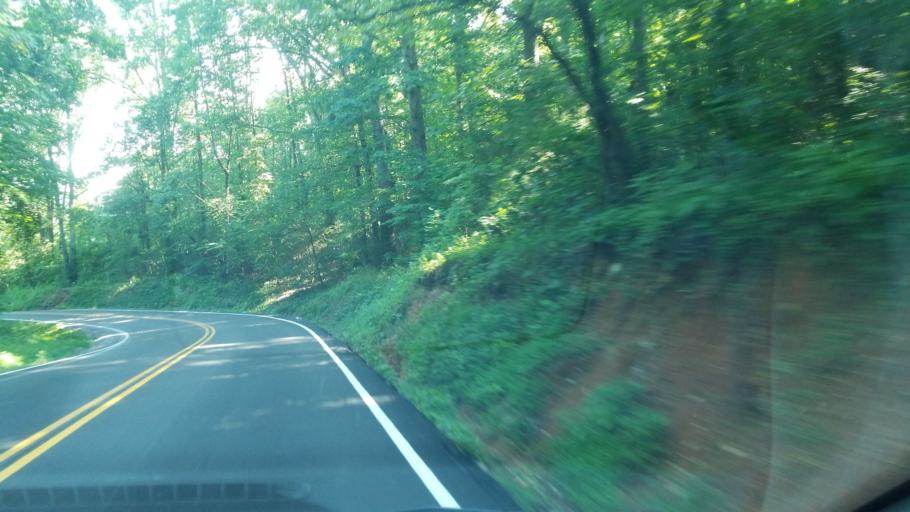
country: US
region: Tennessee
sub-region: Loudon County
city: Loudon
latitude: 35.7911
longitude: -84.3603
